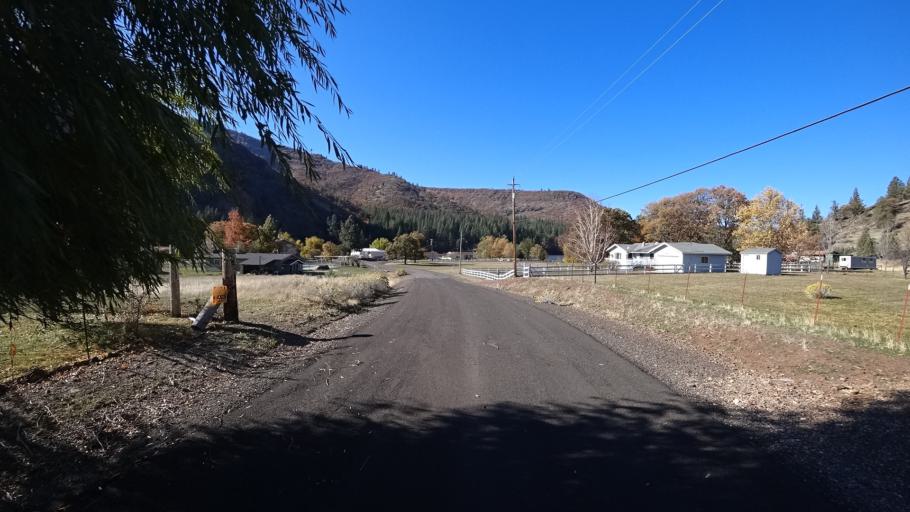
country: US
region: California
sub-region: Siskiyou County
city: Montague
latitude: 41.9660
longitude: -122.2625
